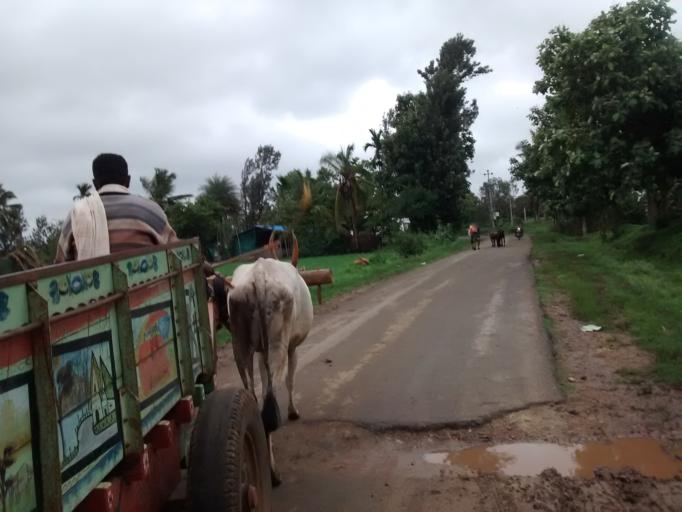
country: IN
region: Karnataka
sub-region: Hassan
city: Hassan
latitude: 12.9281
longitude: 76.1820
